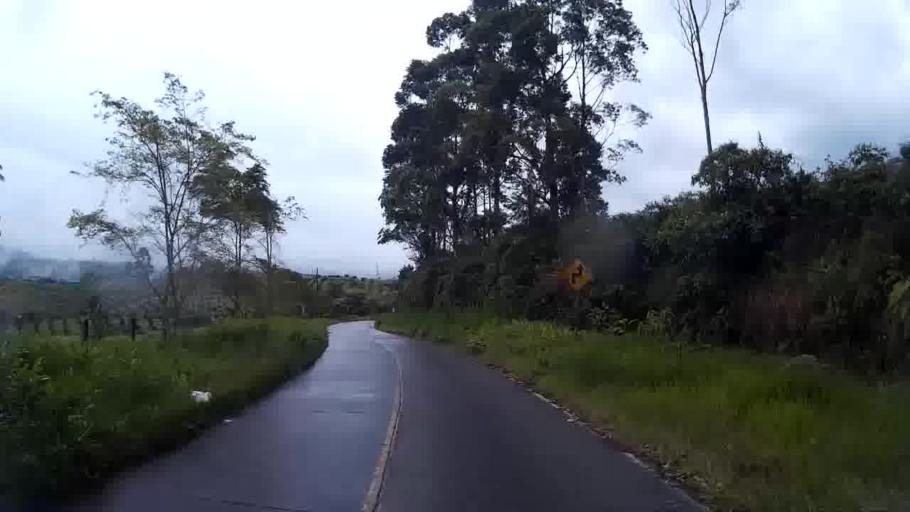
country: CO
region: Quindio
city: Filandia
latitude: 4.6886
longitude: -75.6300
